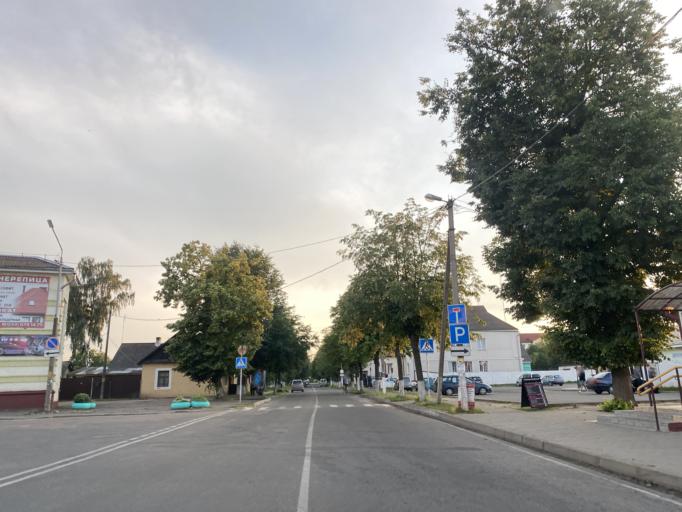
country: BY
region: Brest
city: Ivatsevichy
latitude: 52.7098
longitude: 25.3443
